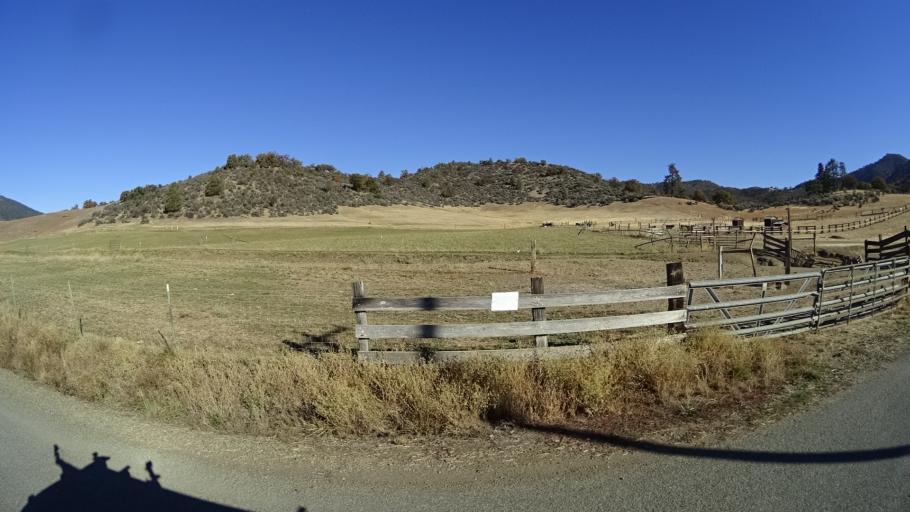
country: US
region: California
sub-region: Siskiyou County
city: Yreka
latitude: 41.5792
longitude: -122.8302
